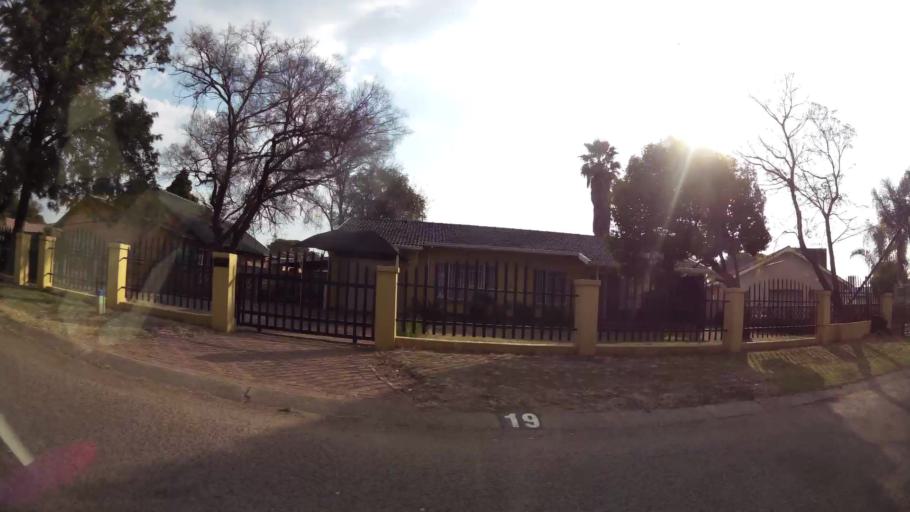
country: ZA
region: Gauteng
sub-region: City of Johannesburg Metropolitan Municipality
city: Modderfontein
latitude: -26.1105
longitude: 28.2075
